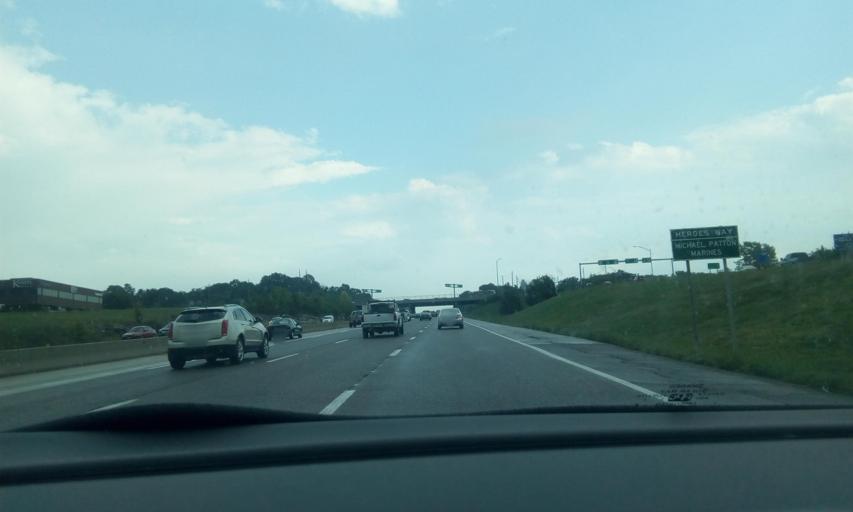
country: US
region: Missouri
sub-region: Saint Louis County
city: Sunset Hills
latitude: 38.5273
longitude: -90.4016
